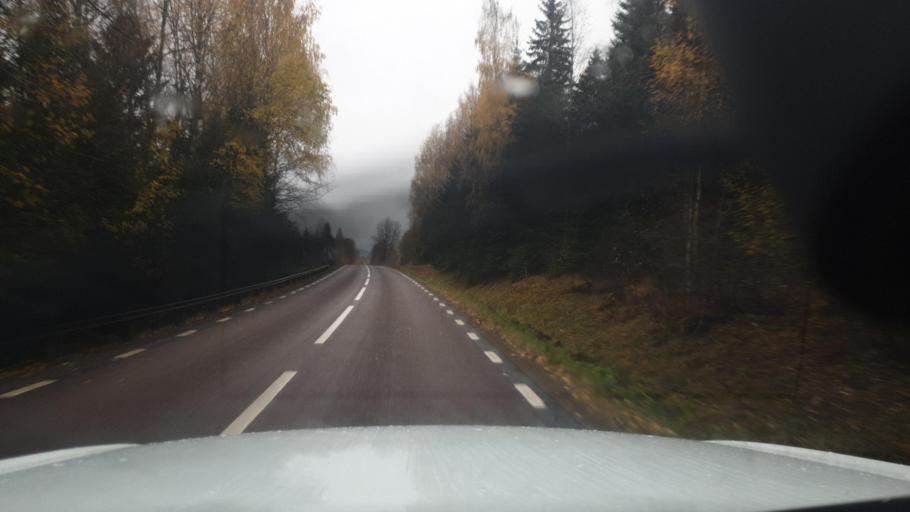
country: SE
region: Vaermland
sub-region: Sunne Kommun
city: Sunne
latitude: 59.9031
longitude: 12.9080
